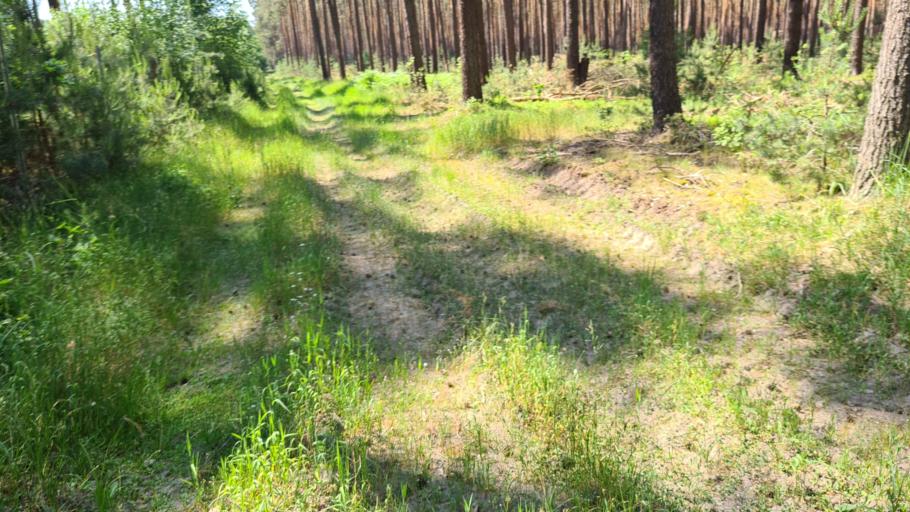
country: DE
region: Brandenburg
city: Schlieben
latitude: 51.7797
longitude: 13.3587
